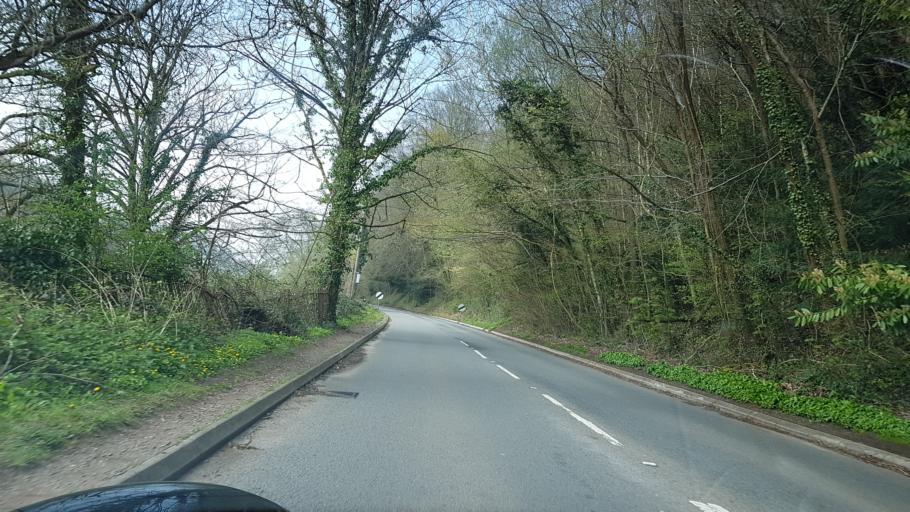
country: GB
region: Wales
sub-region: Monmouthshire
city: Monmouth
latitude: 51.7887
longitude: -2.6752
